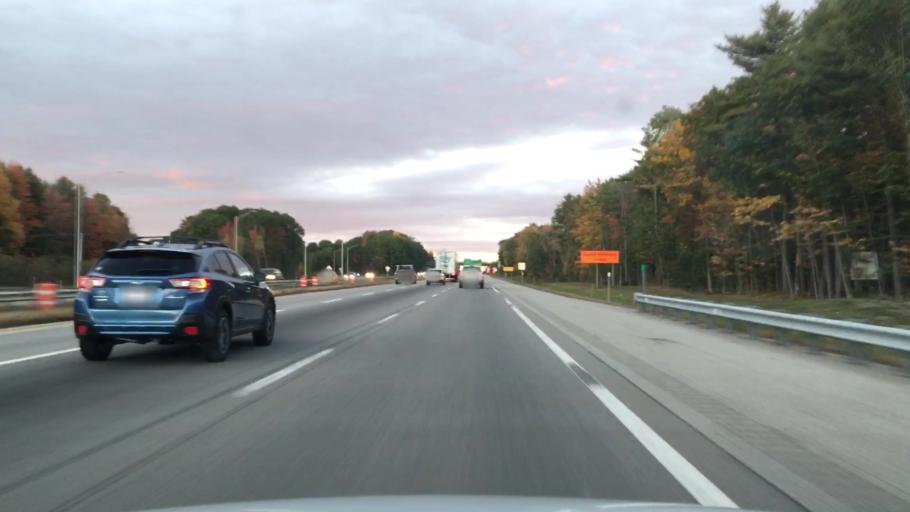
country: US
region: Maine
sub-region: Cumberland County
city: South Portland Gardens
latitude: 43.6176
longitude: -70.3592
